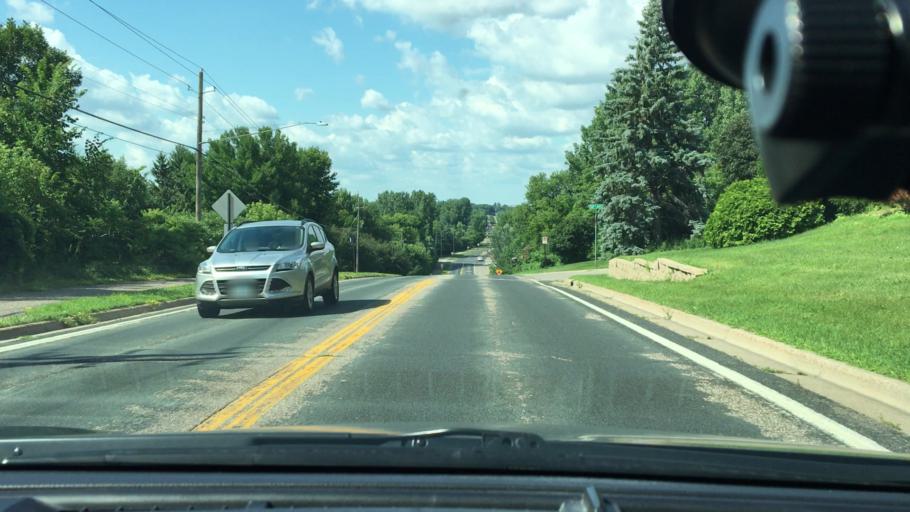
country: US
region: Minnesota
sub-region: Hennepin County
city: New Hope
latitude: 45.0444
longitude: -93.4209
